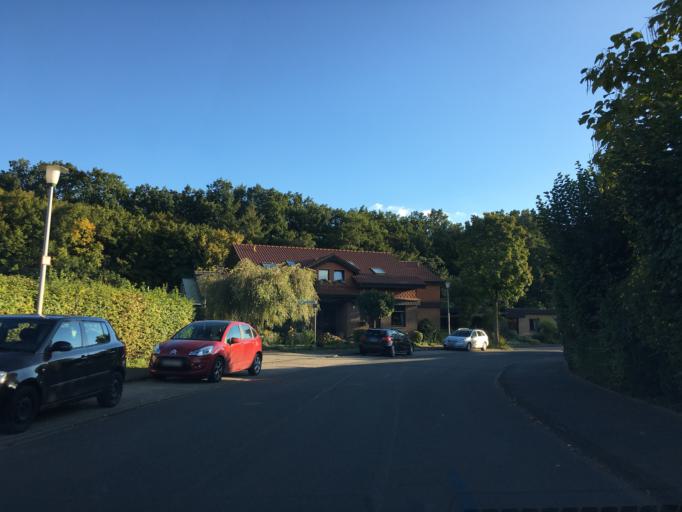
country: DE
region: North Rhine-Westphalia
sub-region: Regierungsbezirk Munster
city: Muenster
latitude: 51.9926
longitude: 7.5570
